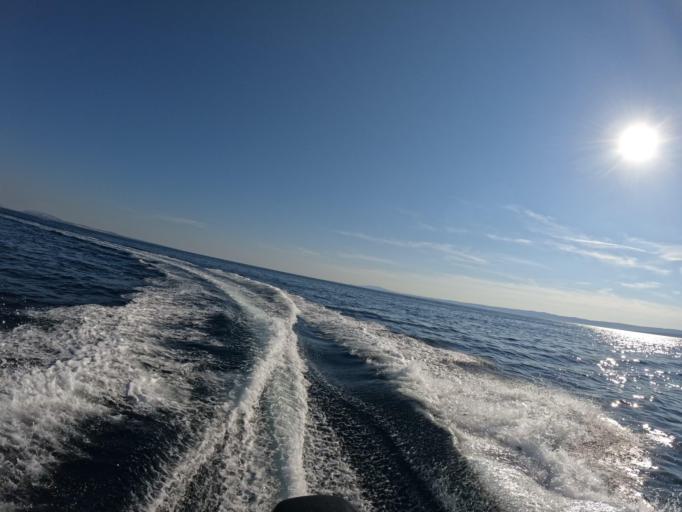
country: HR
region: Primorsko-Goranska
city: Punat
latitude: 44.9681
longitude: 14.6393
